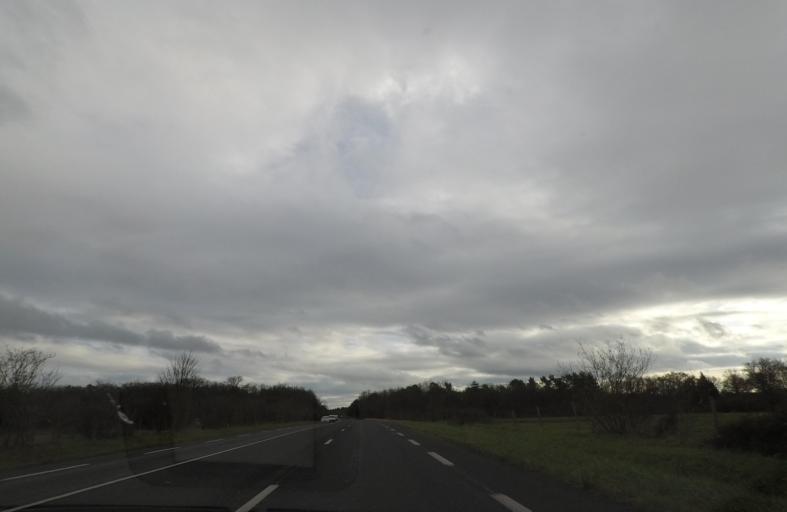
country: FR
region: Centre
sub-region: Departement du Loir-et-Cher
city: Mur-de-Sologne
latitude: 47.3973
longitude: 1.6406
